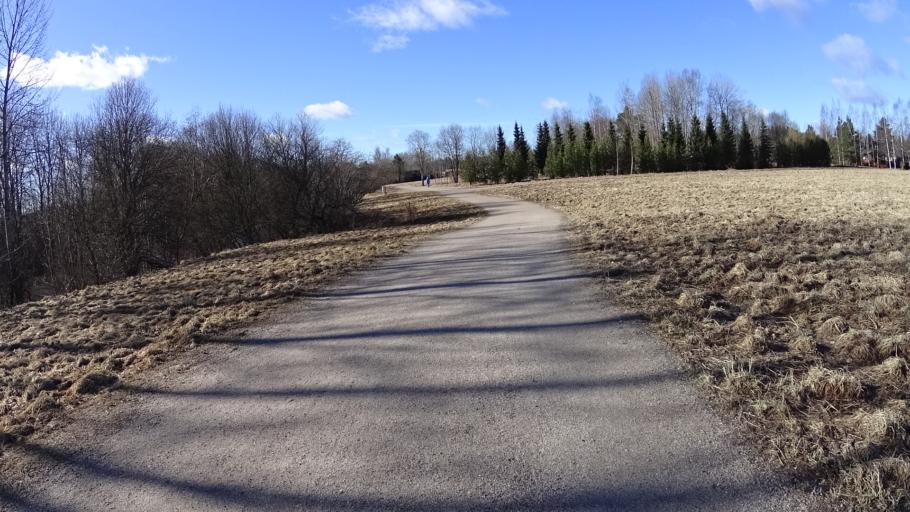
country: FI
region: Uusimaa
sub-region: Helsinki
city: Teekkarikylae
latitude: 60.2759
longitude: 24.8826
